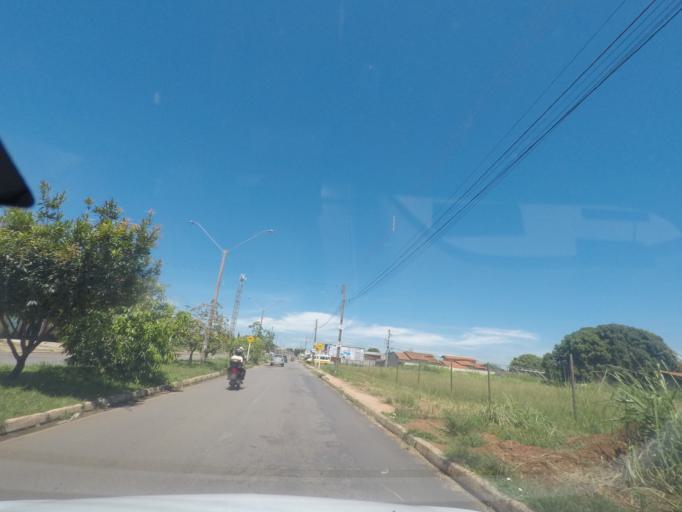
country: BR
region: Goias
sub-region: Aparecida De Goiania
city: Aparecida de Goiania
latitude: -16.7700
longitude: -49.3261
